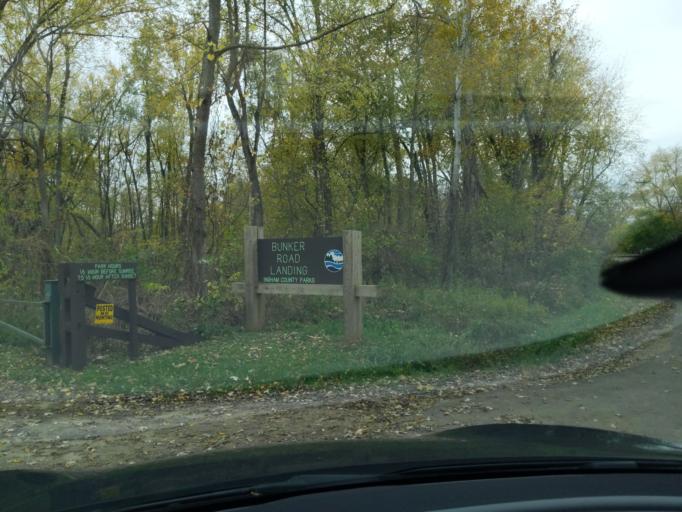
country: US
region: Michigan
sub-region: Eaton County
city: Eaton Rapids
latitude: 42.5530
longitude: -84.6200
